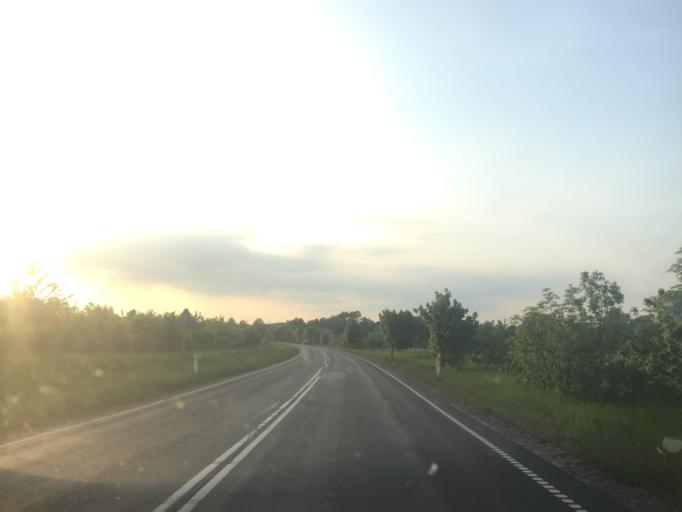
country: DK
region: South Denmark
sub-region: Odense Kommune
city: Neder Holluf
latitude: 55.3483
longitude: 10.4979
